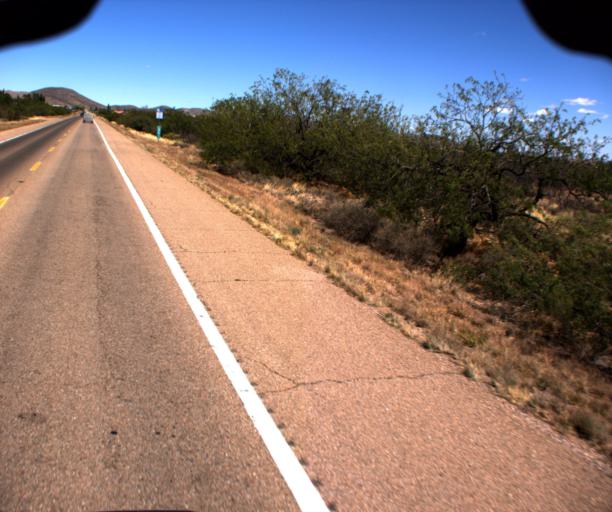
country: US
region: Arizona
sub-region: Cochise County
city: Naco
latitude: 31.3901
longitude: -109.9417
